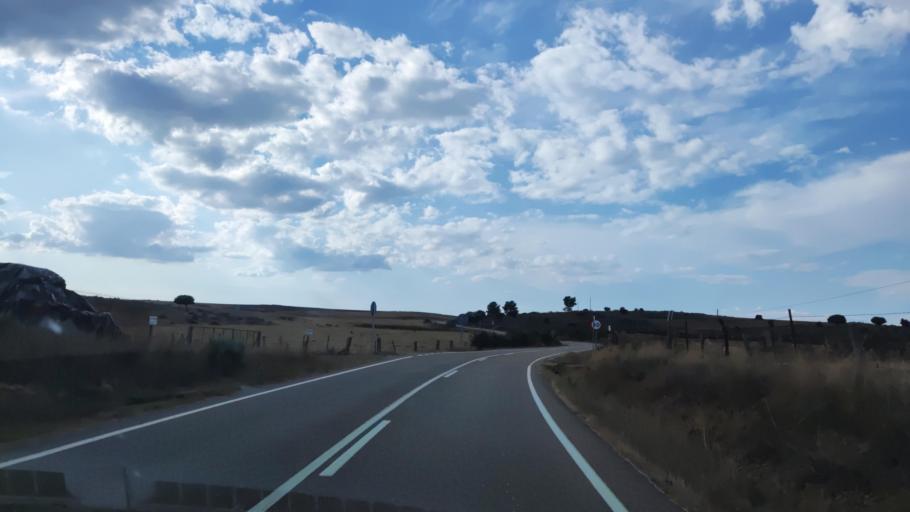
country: ES
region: Castille and Leon
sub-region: Provincia de Salamanca
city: Pastores
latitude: 40.5021
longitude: -6.4996
